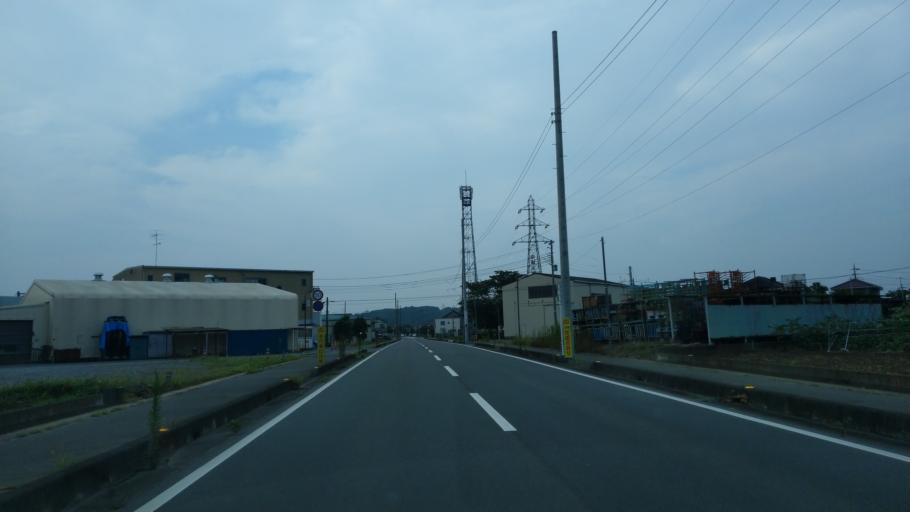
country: JP
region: Saitama
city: Morohongo
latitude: 35.9005
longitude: 139.3316
